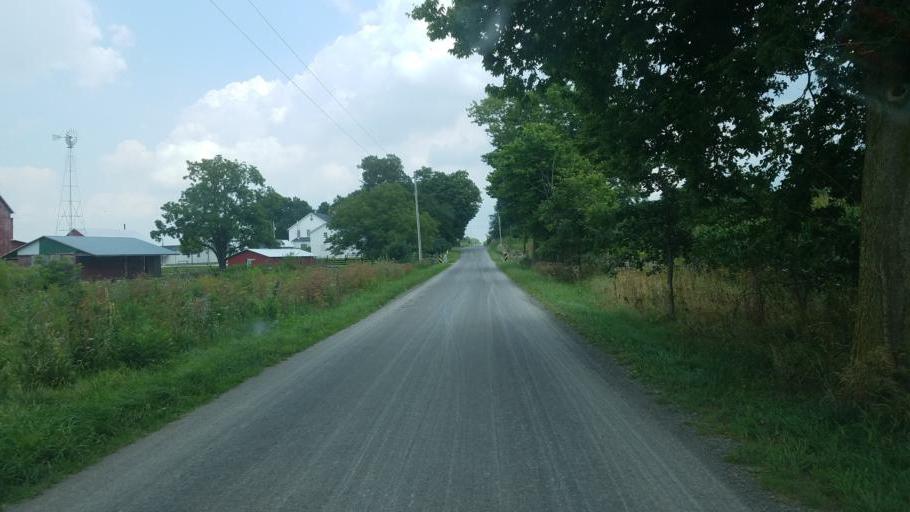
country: US
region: Ohio
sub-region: Hardin County
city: Kenton
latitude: 40.5937
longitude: -83.6193
